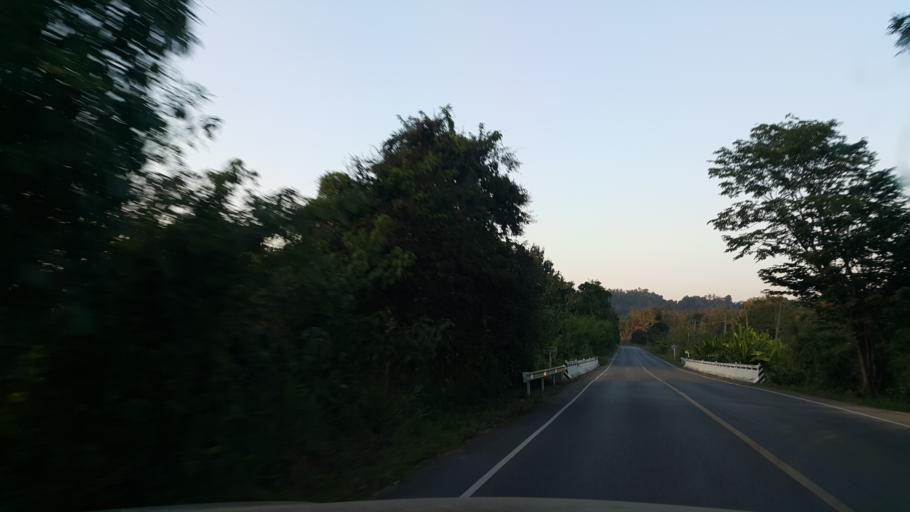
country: TH
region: Phrae
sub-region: Amphoe Wang Chin
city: Wang Chin
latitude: 17.8414
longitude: 99.6418
